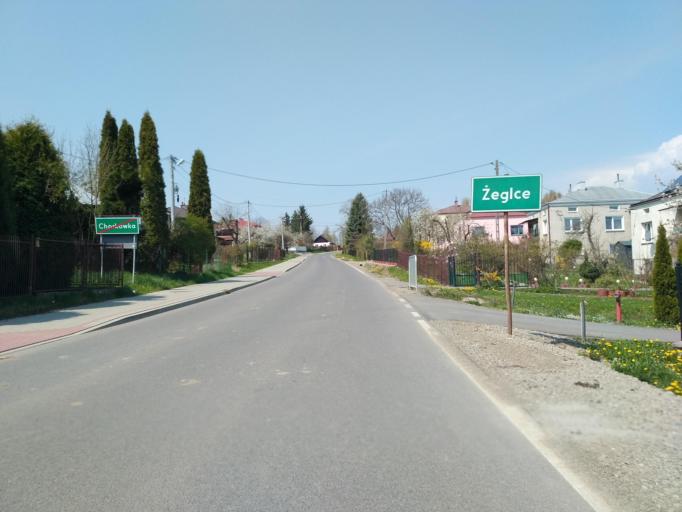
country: PL
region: Subcarpathian Voivodeship
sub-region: Powiat krosnienski
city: Chorkowka
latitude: 49.6533
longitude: 21.6684
